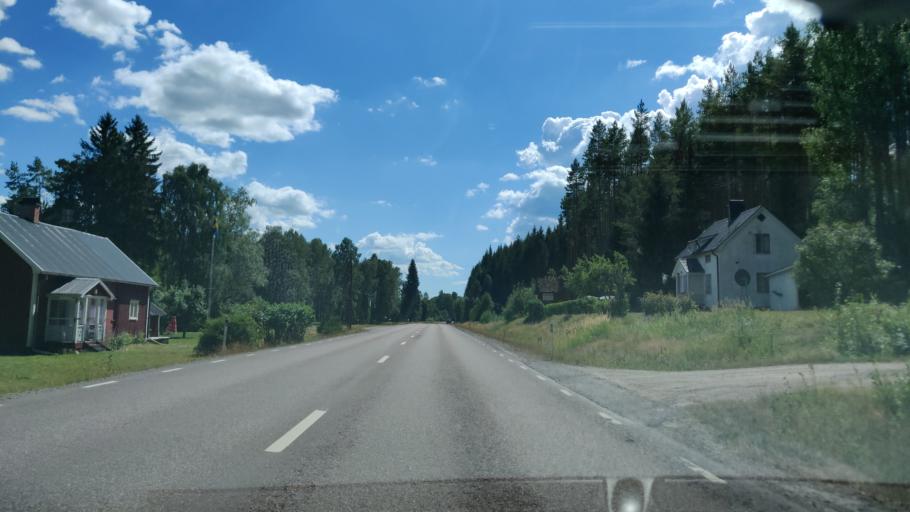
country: SE
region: Vaermland
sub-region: Hagfors Kommun
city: Ekshaerad
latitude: 60.1909
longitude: 13.4976
